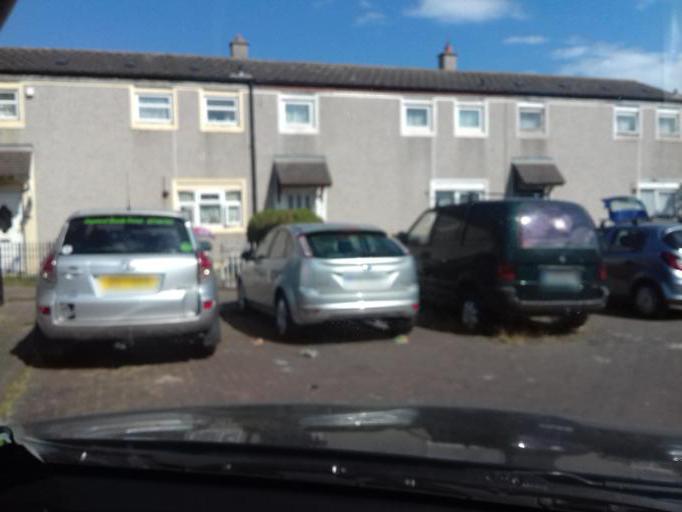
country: IE
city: Darndale
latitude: 53.3991
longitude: -6.1924
